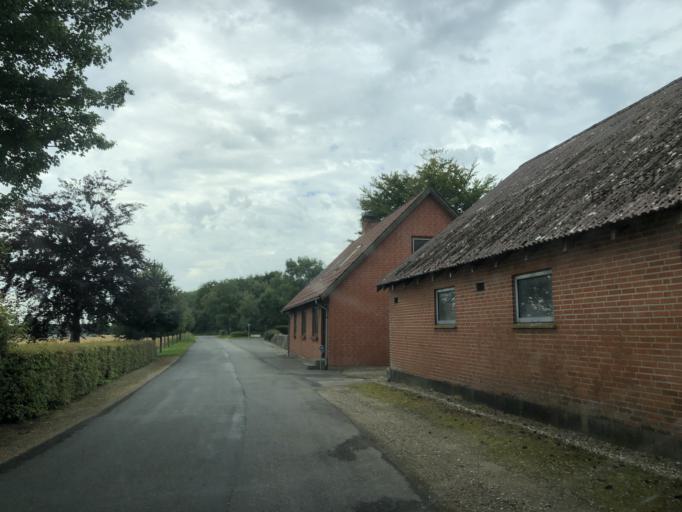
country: DK
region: Central Jutland
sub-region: Holstebro Kommune
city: Holstebro
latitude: 56.3860
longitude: 8.5221
